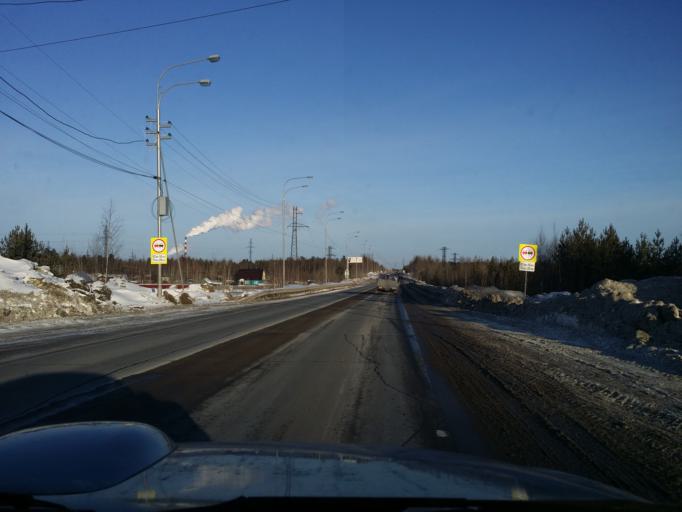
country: RU
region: Khanty-Mansiyskiy Avtonomnyy Okrug
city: Izluchinsk
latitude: 60.9650
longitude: 76.8505
